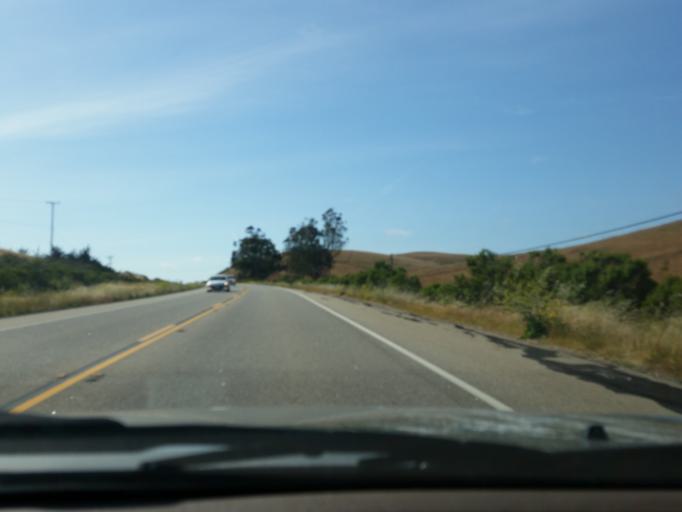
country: US
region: California
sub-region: San Luis Obispo County
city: Cambria
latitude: 35.5017
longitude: -121.0136
